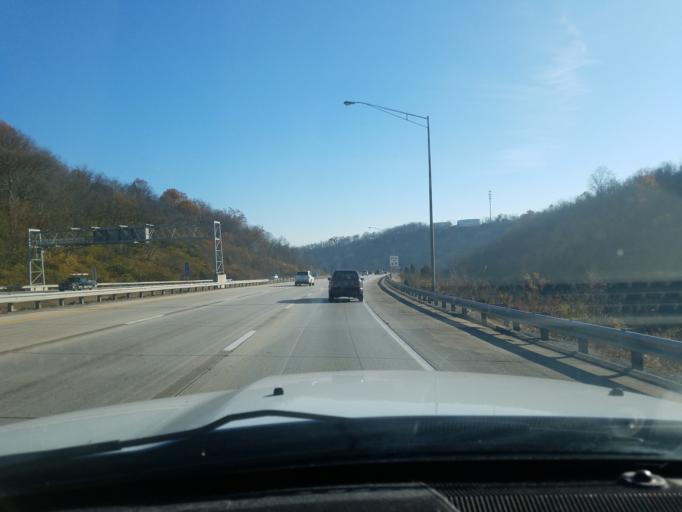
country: US
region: Kentucky
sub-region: Kenton County
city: Lakeside Park
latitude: 39.0267
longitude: -84.5535
